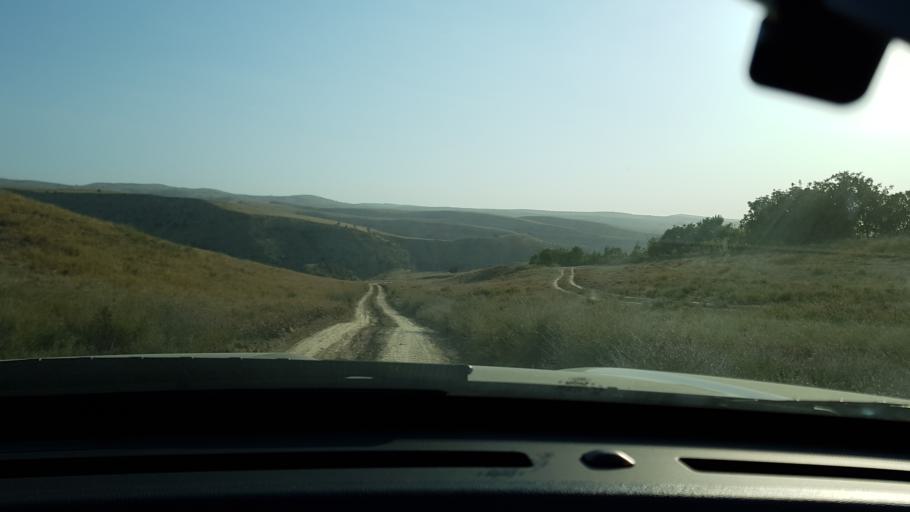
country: TM
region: Ahal
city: Baharly
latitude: 38.4093
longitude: 56.9131
